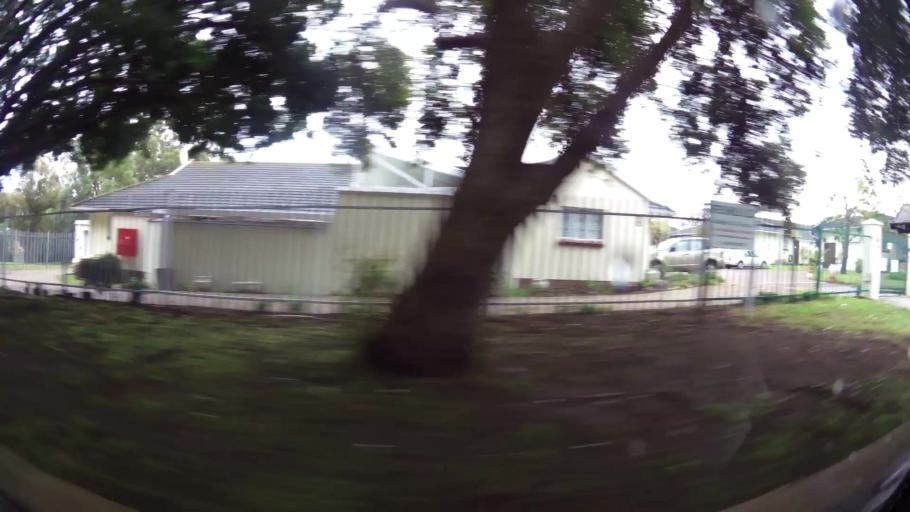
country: ZA
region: Eastern Cape
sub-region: Nelson Mandela Bay Metropolitan Municipality
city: Port Elizabeth
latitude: -33.9770
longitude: 25.5845
